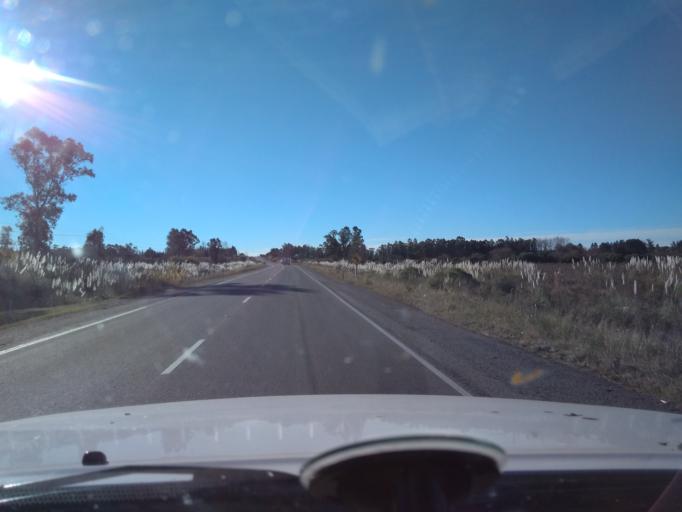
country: UY
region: Canelones
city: Sauce
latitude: -34.5971
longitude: -56.0509
